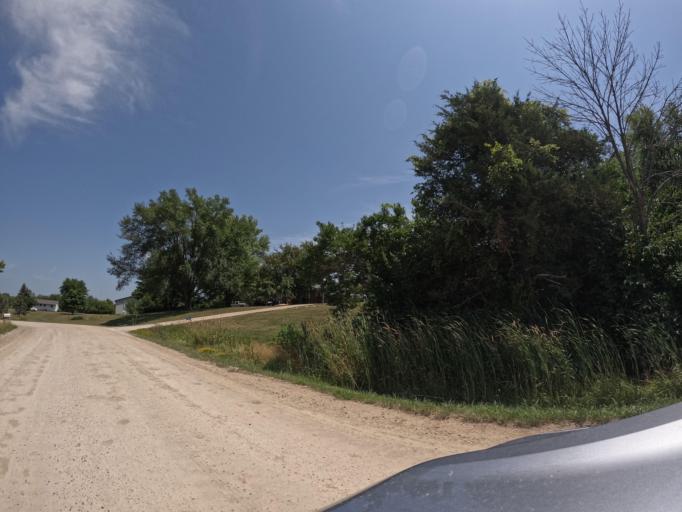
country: US
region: Iowa
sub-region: Henry County
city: Mount Pleasant
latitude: 40.9388
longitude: -91.5795
